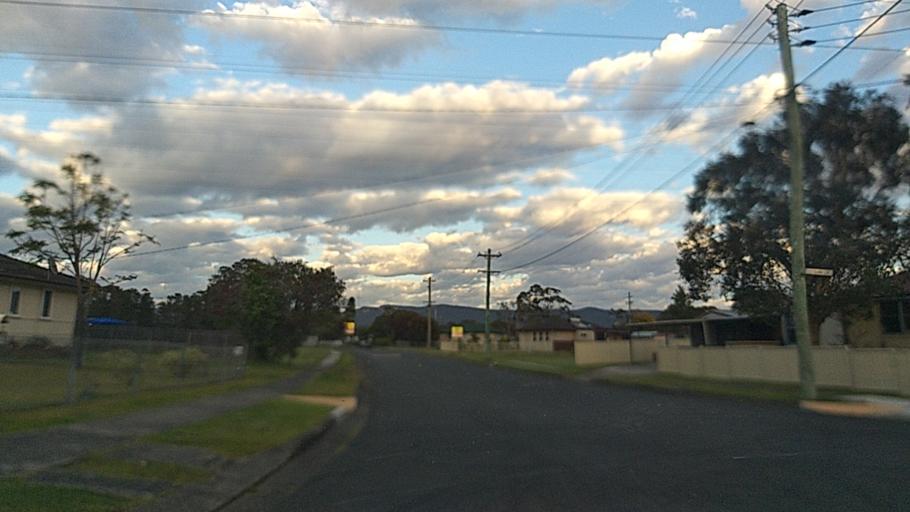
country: AU
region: New South Wales
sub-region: Wollongong
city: Koonawarra
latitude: -34.5002
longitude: 150.8104
